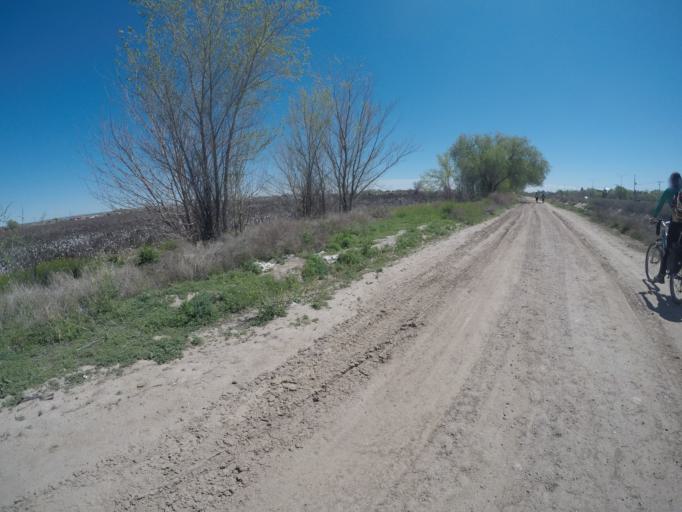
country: US
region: Texas
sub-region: El Paso County
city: Socorro Mission Number 1 Colonia
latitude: 31.6148
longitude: -106.3172
